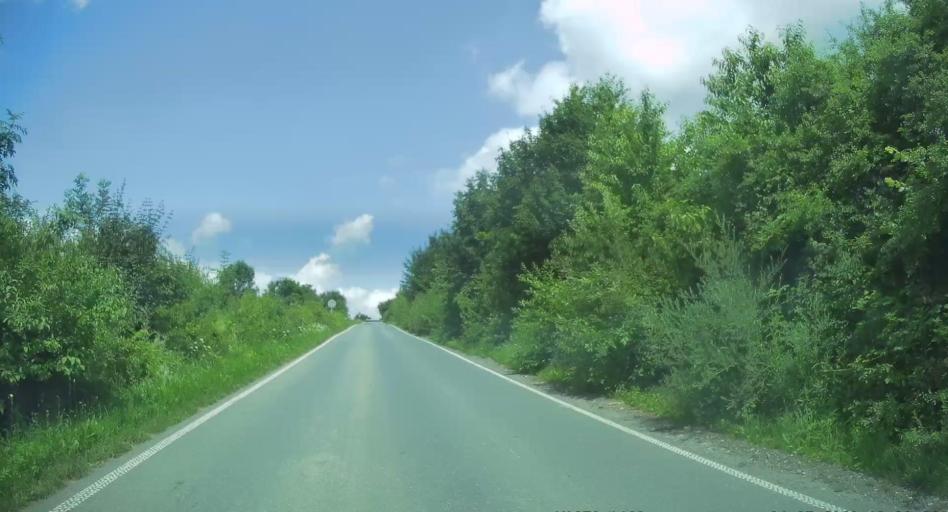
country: PL
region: Lesser Poland Voivodeship
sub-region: Powiat nowosadecki
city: Korzenna
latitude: 49.7048
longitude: 20.7638
